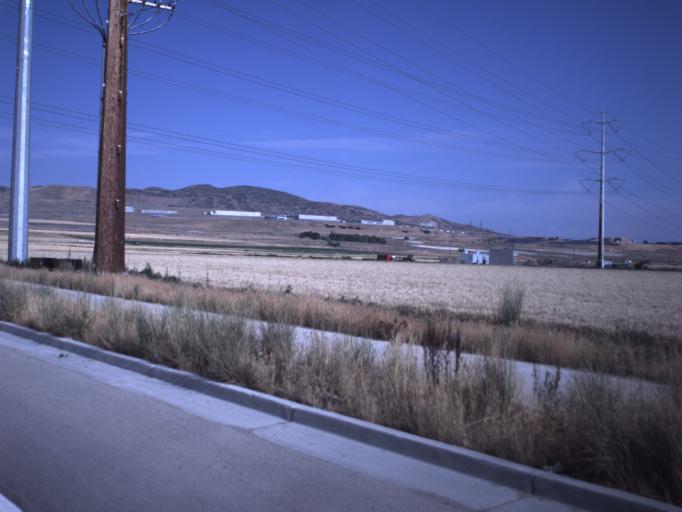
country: US
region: Utah
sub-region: Utah County
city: Lehi
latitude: 40.4132
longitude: -111.9087
